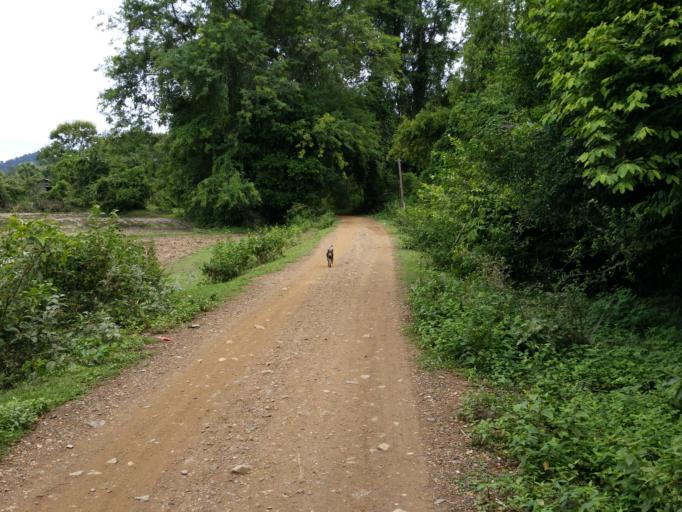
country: LA
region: Champasak
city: Khong
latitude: 13.9612
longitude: 105.9220
